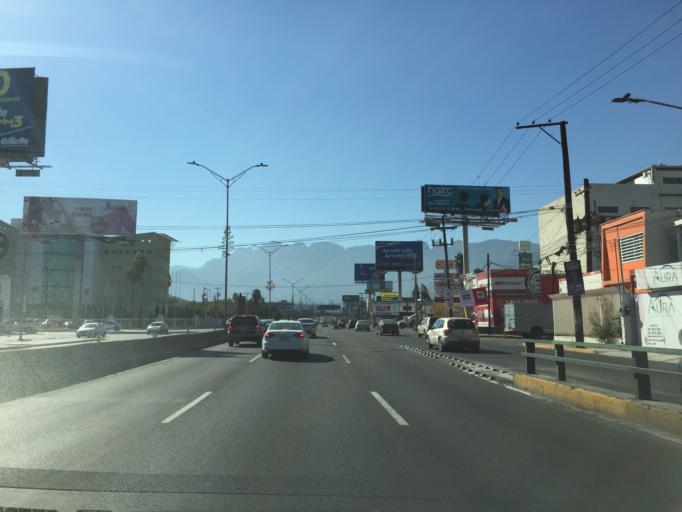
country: MX
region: Nuevo Leon
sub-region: Monterrey
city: Monterrey
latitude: 25.6953
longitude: -100.3514
